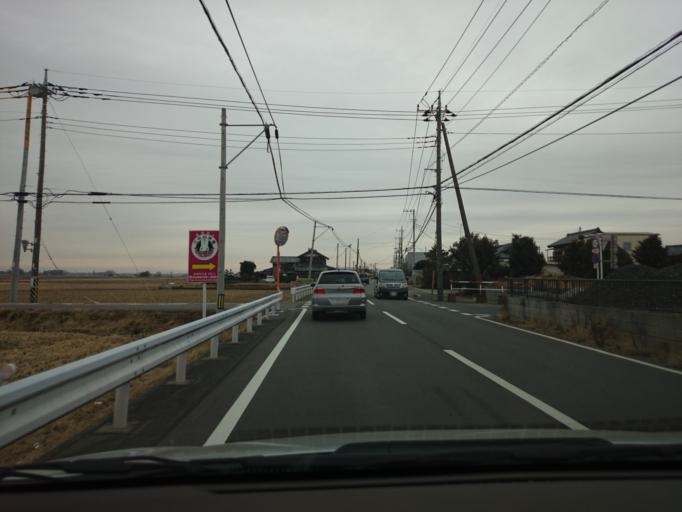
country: JP
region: Saitama
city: Kazo
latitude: 36.1012
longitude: 139.6157
